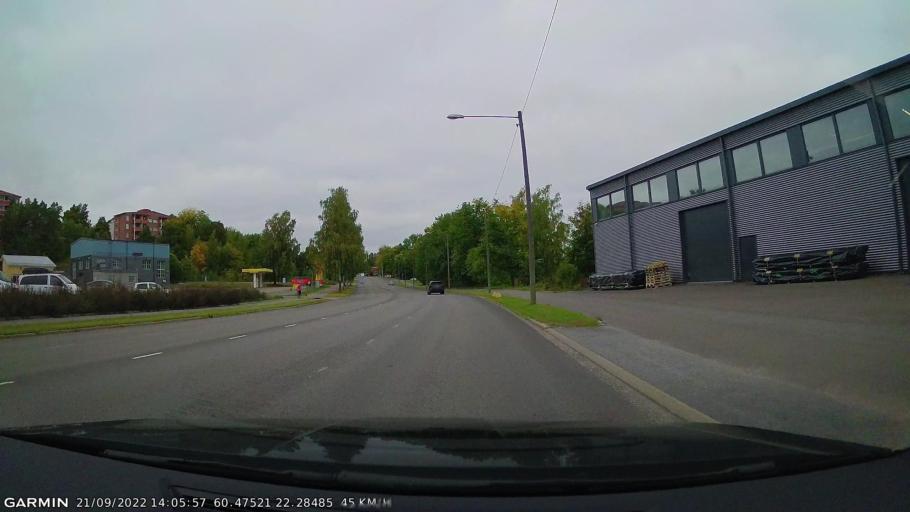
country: FI
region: Varsinais-Suomi
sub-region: Turku
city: Turku
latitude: 60.4752
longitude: 22.2846
